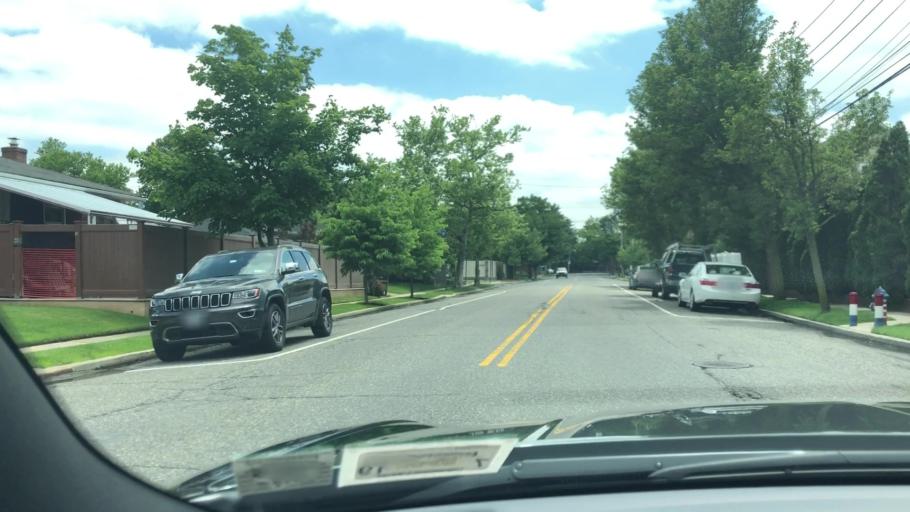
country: US
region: New York
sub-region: Richmond County
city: Staten Island
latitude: 40.5682
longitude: -74.1338
